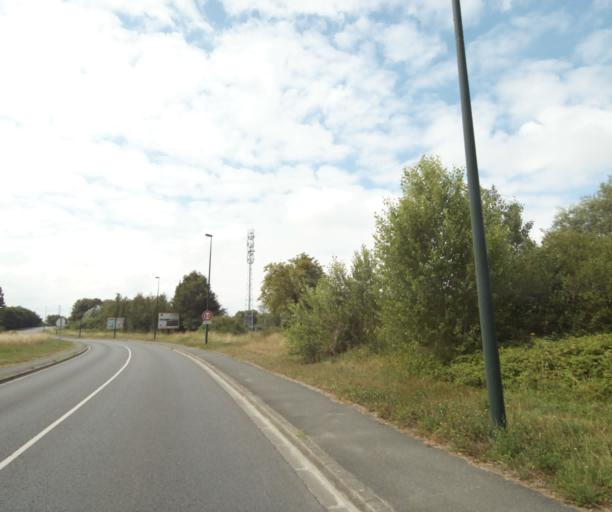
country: FR
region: Centre
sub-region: Departement du Loiret
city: Checy
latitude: 47.8989
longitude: 2.0412
